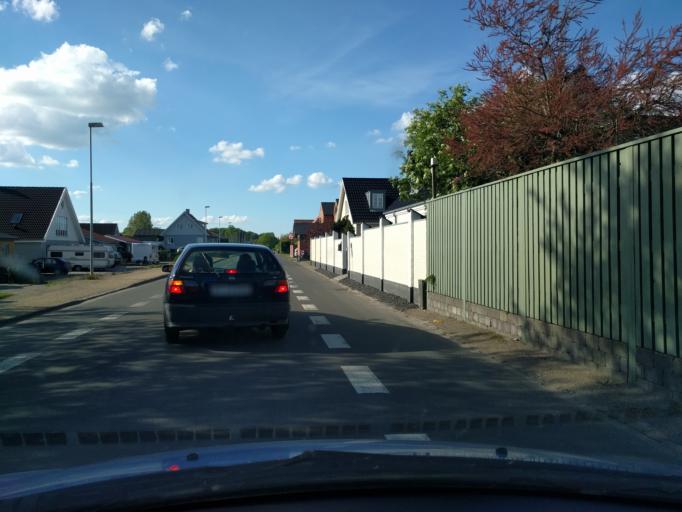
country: DK
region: South Denmark
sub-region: Nyborg Kommune
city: Nyborg
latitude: 55.3118
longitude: 10.8157
